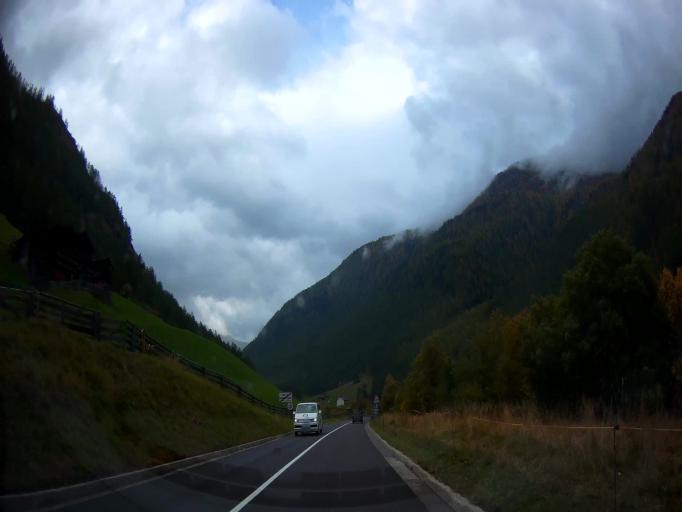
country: IT
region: Trentino-Alto Adige
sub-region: Bolzano
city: Senales
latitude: 46.7199
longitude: 10.8647
